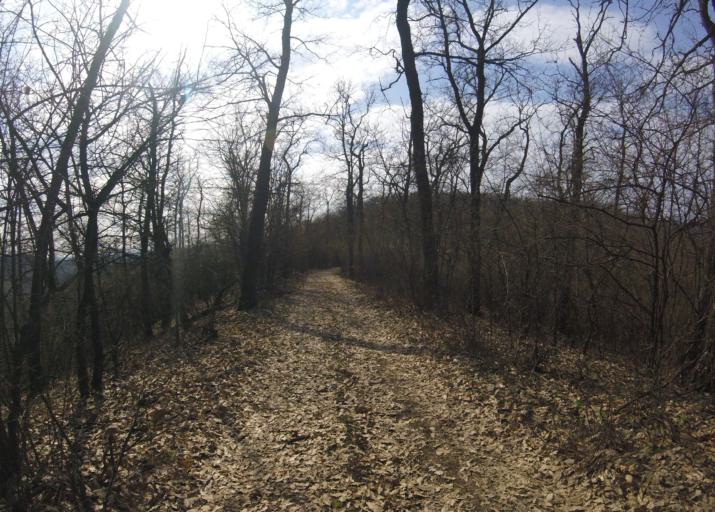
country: HU
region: Heves
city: Belapatfalva
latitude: 48.0026
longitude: 20.3348
